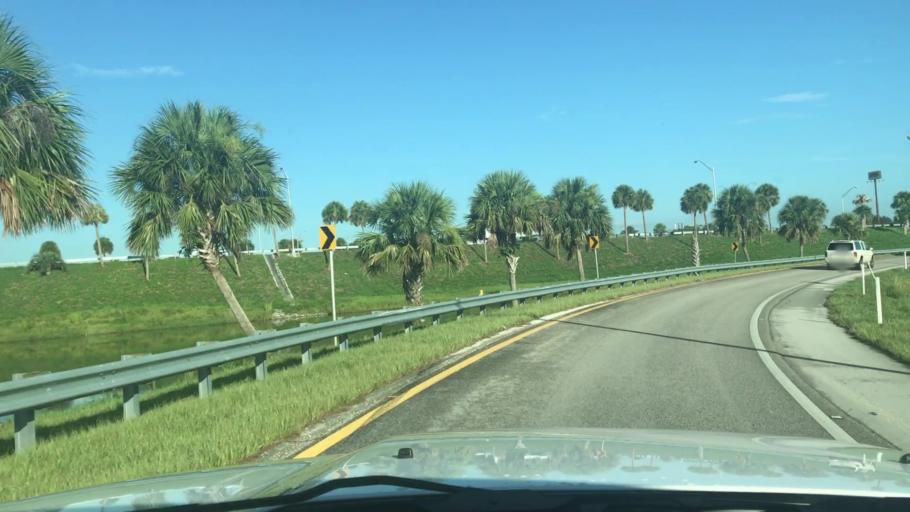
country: US
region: Florida
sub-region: Saint Lucie County
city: Fort Pierce South
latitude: 27.4170
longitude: -80.3870
